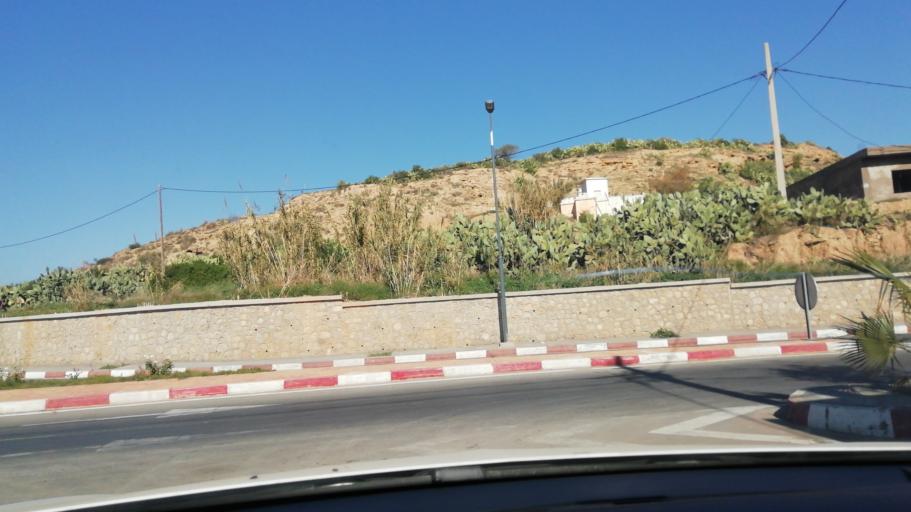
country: DZ
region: Tlemcen
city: Remchi
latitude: 35.0521
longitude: -1.5404
